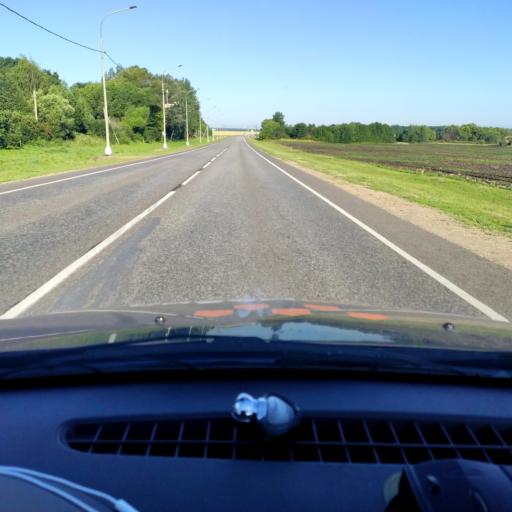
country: RU
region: Orjol
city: Pokrovskoye
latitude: 52.6199
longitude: 36.7388
